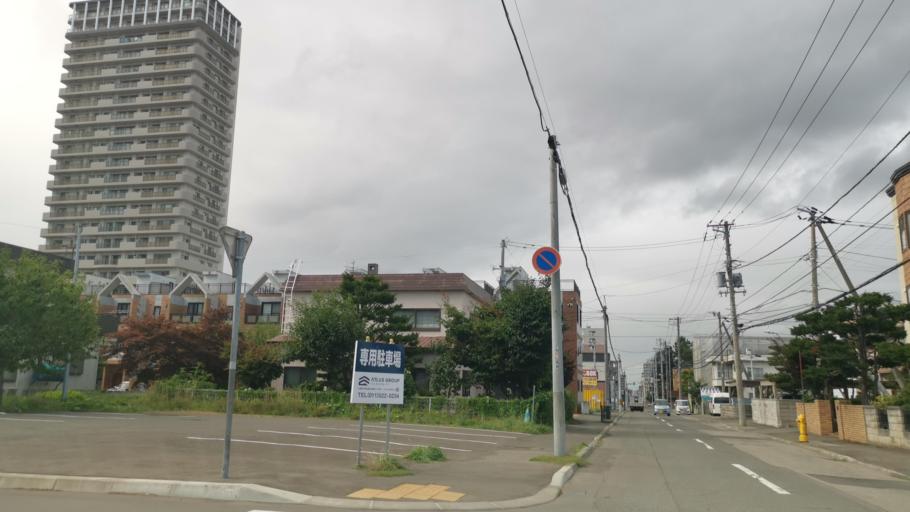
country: JP
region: Hokkaido
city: Sapporo
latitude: 43.0327
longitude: 141.3432
